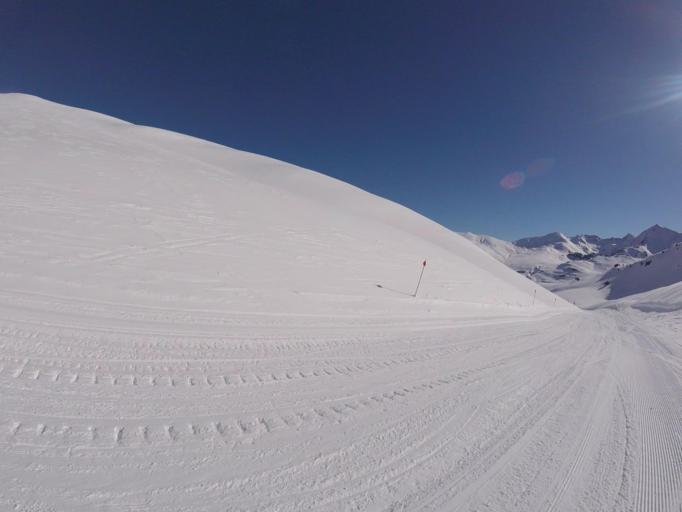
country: ES
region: Catalonia
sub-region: Provincia de Lleida
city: Vielha
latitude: 42.7246
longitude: 0.9421
